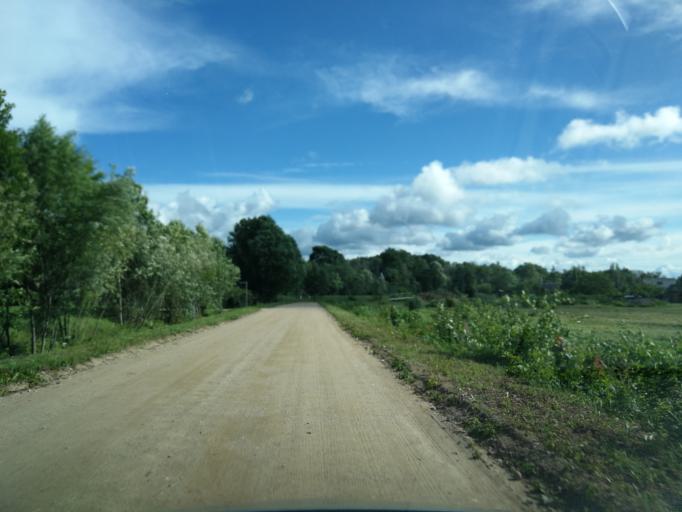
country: LV
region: Adazi
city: Adazi
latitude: 57.0959
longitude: 24.3243
